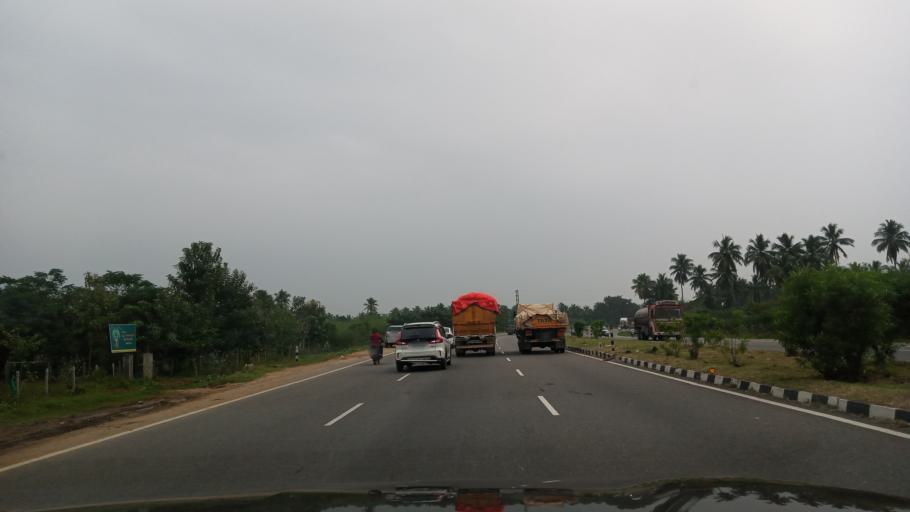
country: IN
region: Tamil Nadu
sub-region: Vellore
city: Arcot
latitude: 12.9357
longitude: 79.2563
